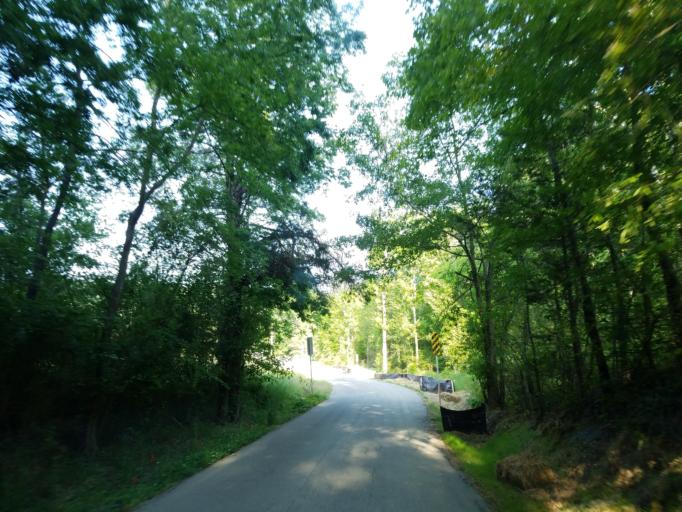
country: US
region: Georgia
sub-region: Floyd County
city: Shannon
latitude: 34.4953
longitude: -85.1163
